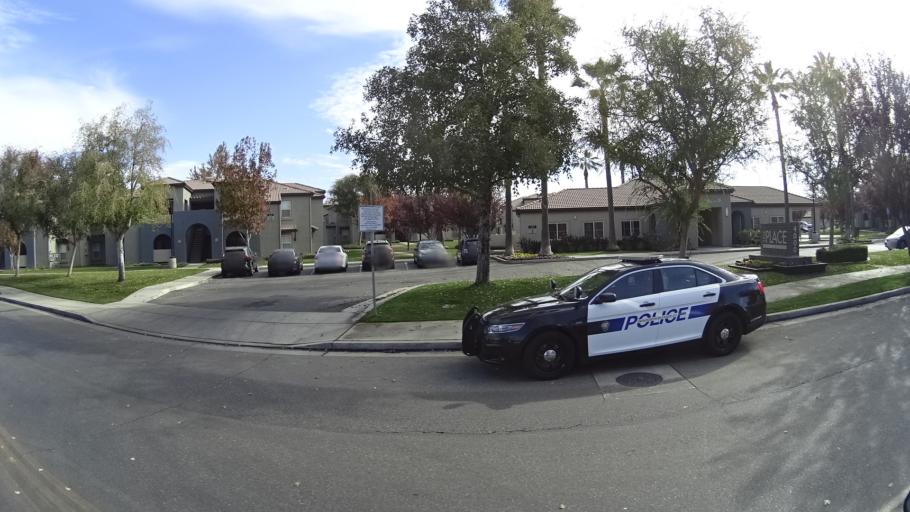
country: US
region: California
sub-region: Kern County
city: Greenacres
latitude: 35.3963
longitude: -119.0887
